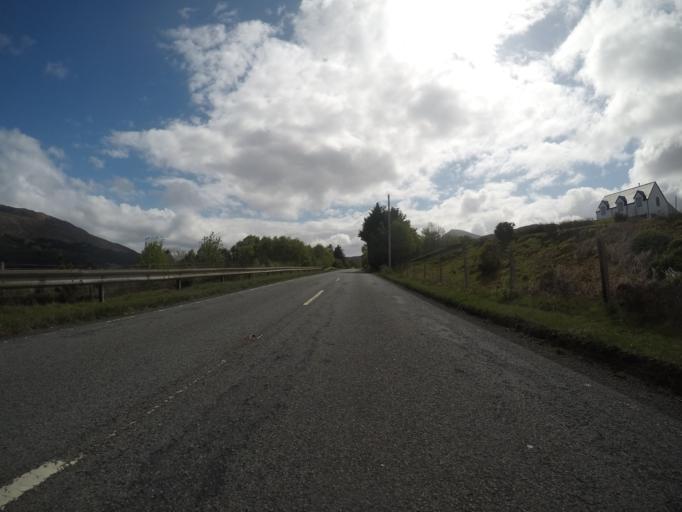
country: GB
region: Scotland
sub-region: Highland
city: Portree
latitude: 57.2806
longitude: -6.0108
